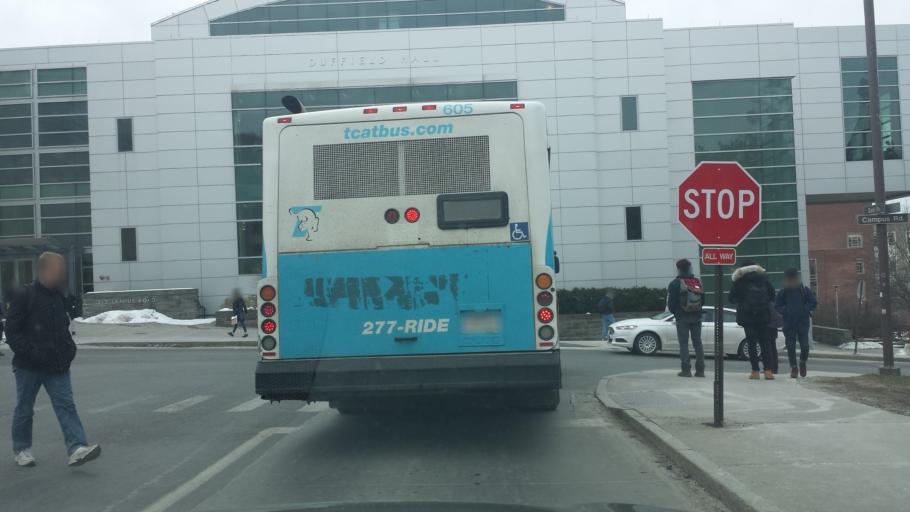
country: US
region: New York
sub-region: Tompkins County
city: East Ithaca
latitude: 42.4454
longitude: -76.4827
